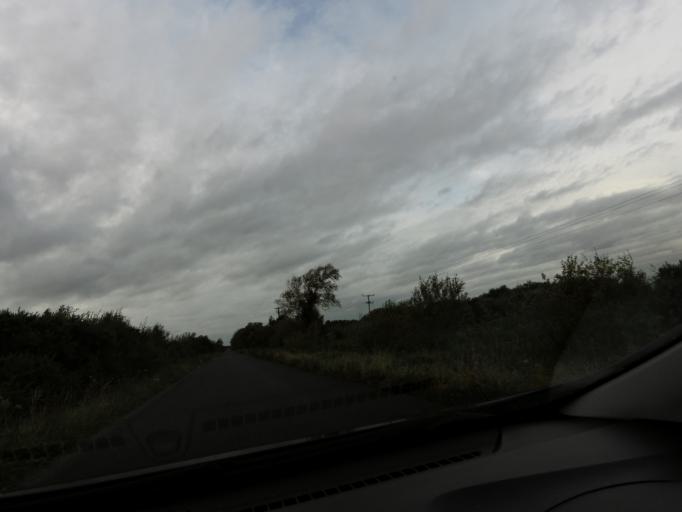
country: IE
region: Leinster
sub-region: Uibh Fhaili
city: Ferbane
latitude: 53.2362
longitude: -7.8258
